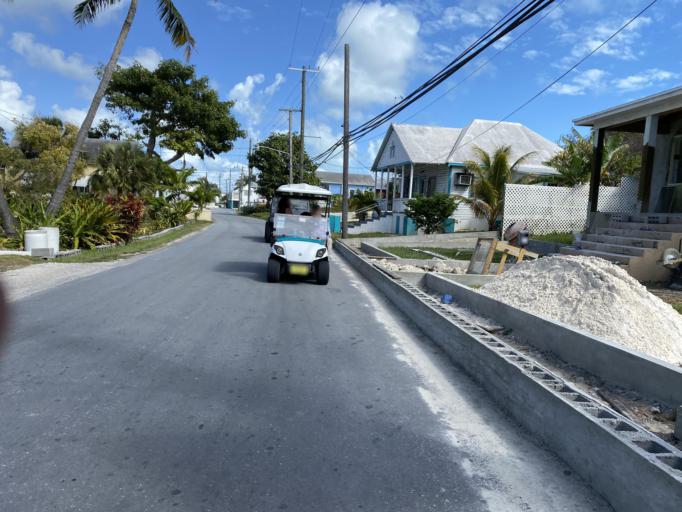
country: BS
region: Spanish Wells
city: Spanish Wells
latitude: 25.5438
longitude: -76.7509
